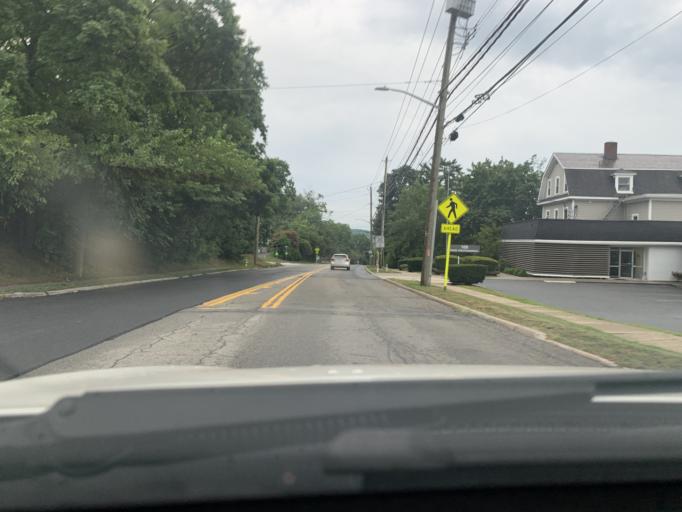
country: US
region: New York
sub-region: Westchester County
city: Ossining
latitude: 41.1543
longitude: -73.8599
